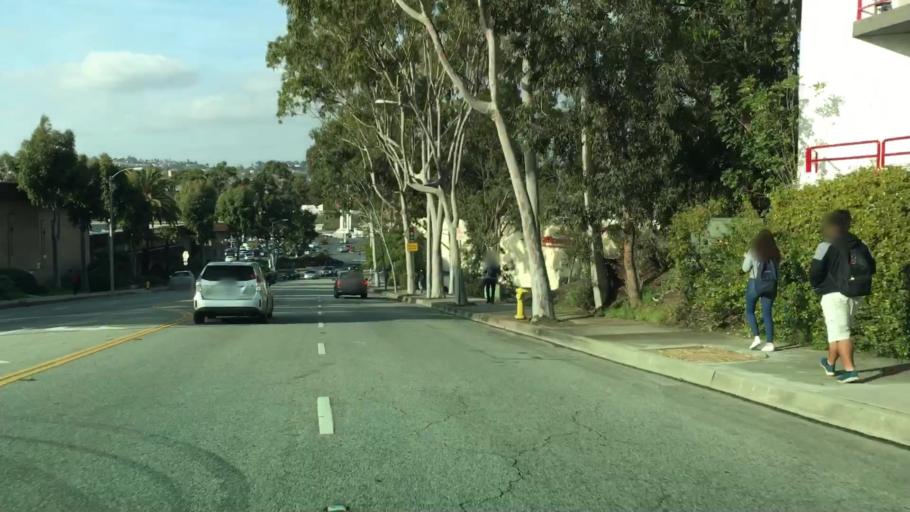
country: US
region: California
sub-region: Los Angeles County
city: Montebello
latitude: 34.0297
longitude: -118.1246
